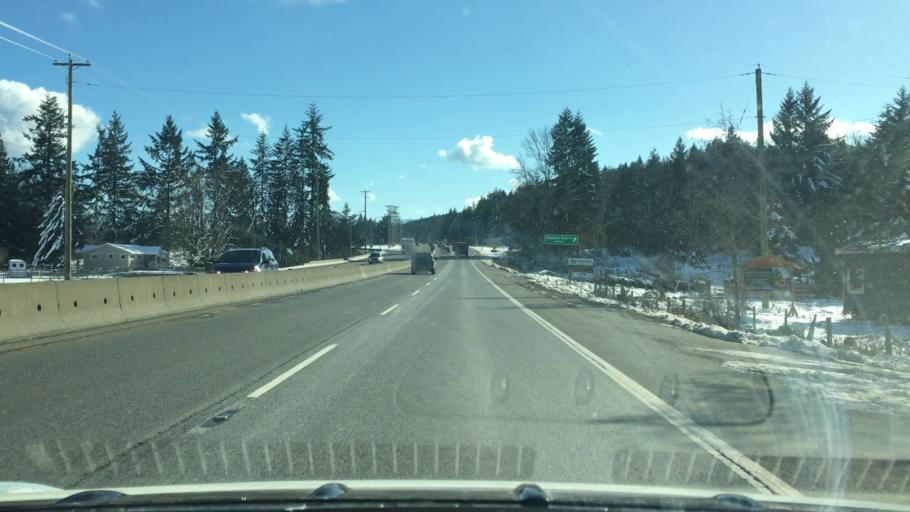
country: CA
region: British Columbia
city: Nanaimo
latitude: 49.0786
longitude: -123.8823
